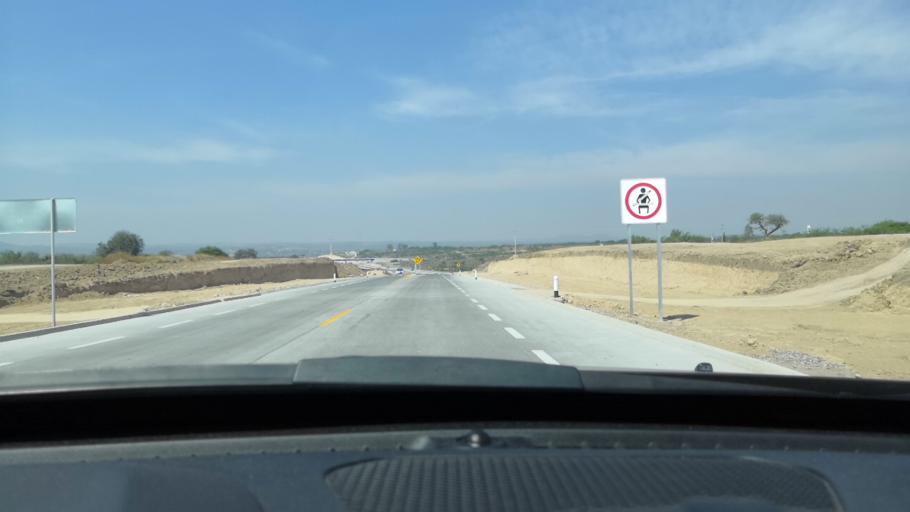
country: MX
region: Guanajuato
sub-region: San Francisco del Rincon
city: Estacion de San Francisco
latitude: 21.0870
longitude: -101.8146
